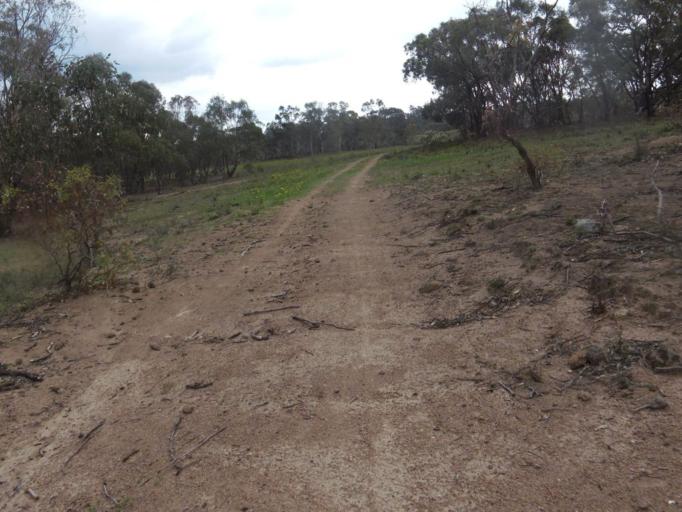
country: AU
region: Australian Capital Territory
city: Forrest
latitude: -35.3505
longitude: 149.1229
